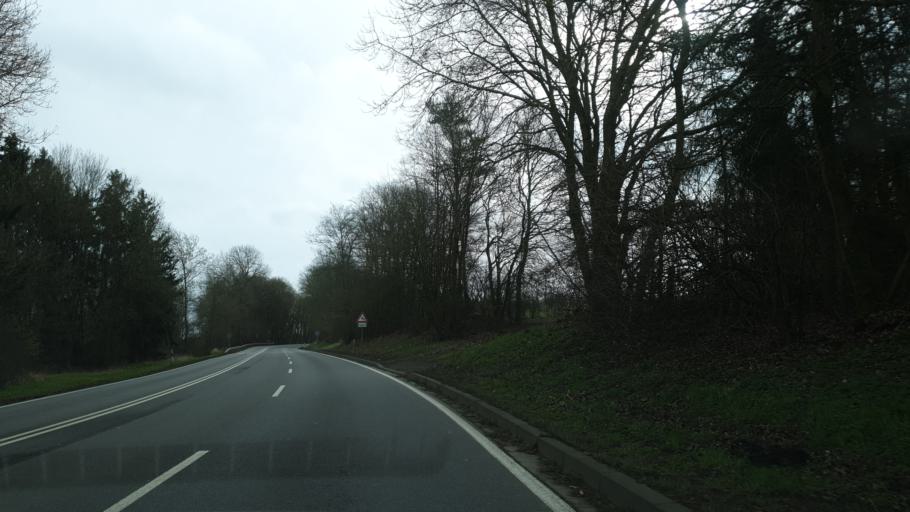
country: DE
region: Rheinland-Pfalz
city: Halsenbach
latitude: 50.1745
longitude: 7.5676
